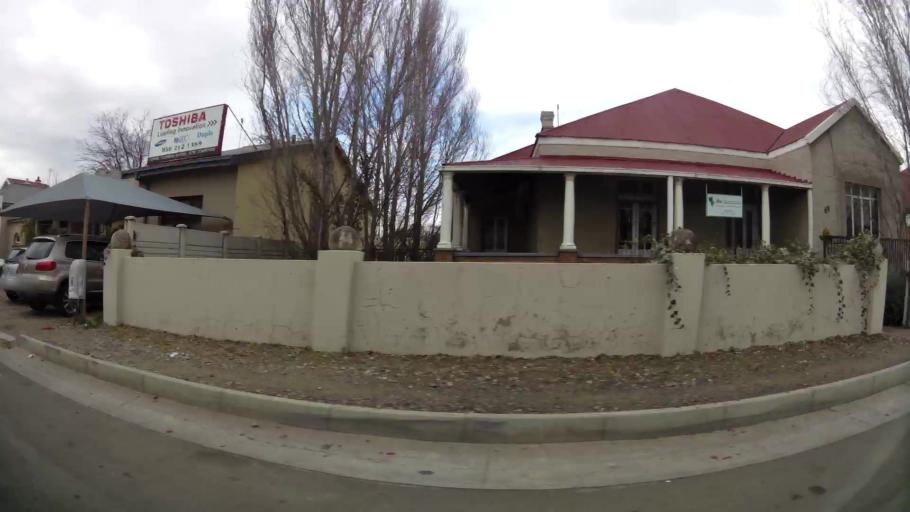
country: ZA
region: Orange Free State
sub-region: Fezile Dabi District Municipality
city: Kroonstad
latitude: -27.6597
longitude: 27.2417
